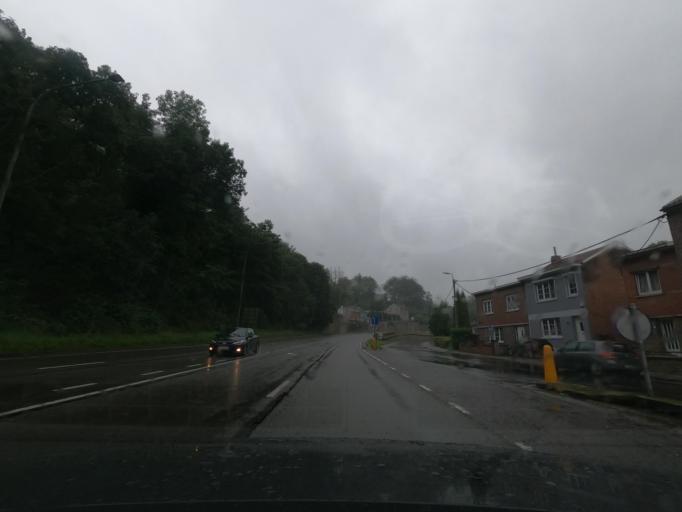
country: BE
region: Wallonia
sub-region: Province de Liege
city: Flemalle-Haute
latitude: 50.6008
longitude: 5.4584
